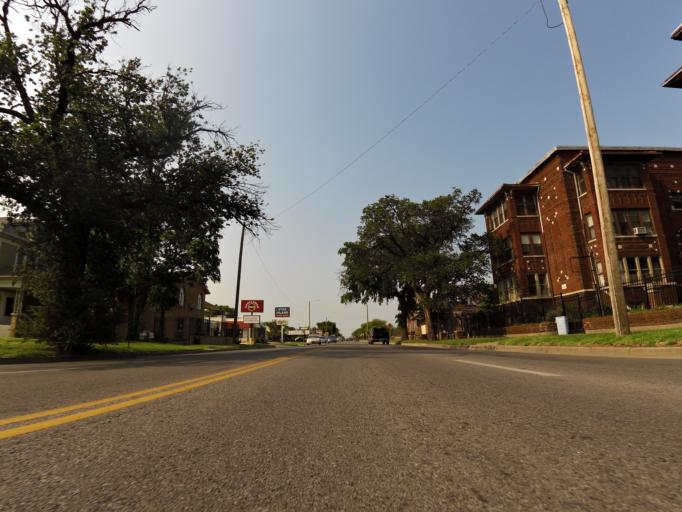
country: US
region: Kansas
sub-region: Sedgwick County
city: Wichita
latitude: 37.6992
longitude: -97.3356
